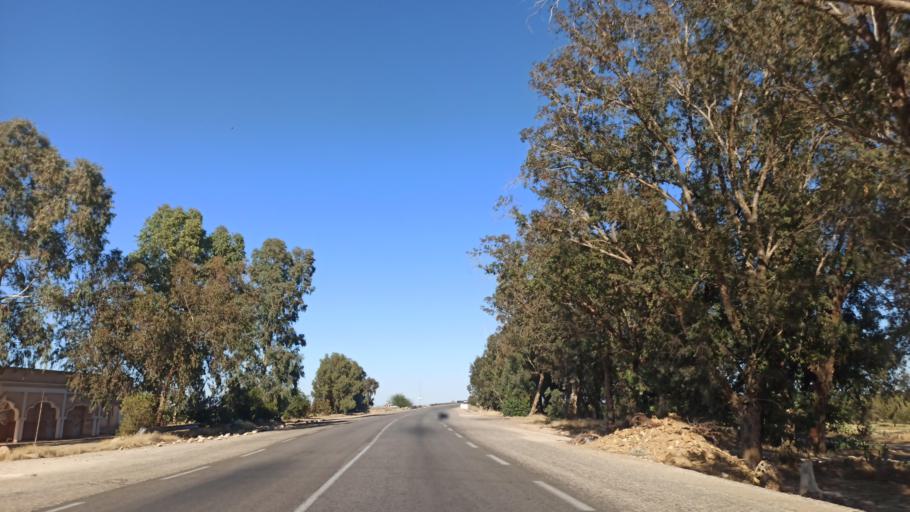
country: TN
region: Sidi Bu Zayd
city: Jilma
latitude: 35.2201
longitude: 9.3811
